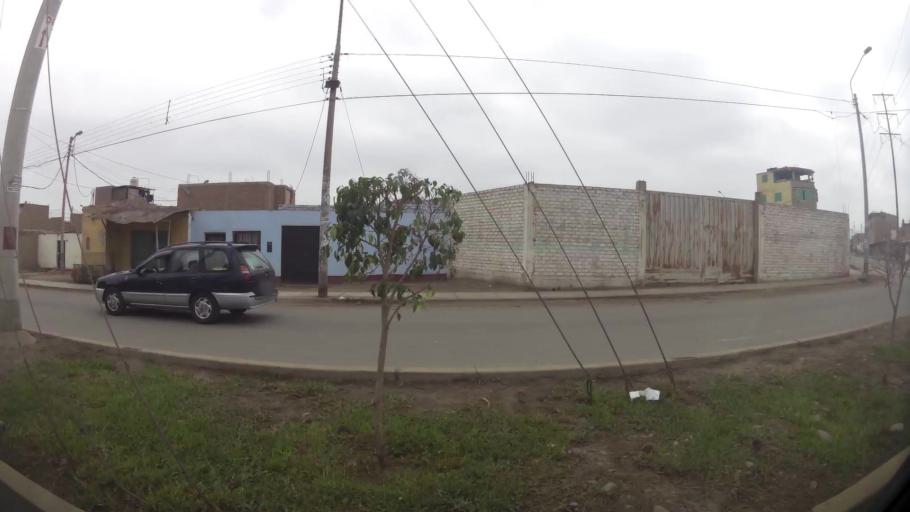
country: PE
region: Lima
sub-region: Provincia de Huaral
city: Huaral
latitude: -11.4989
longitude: -77.1999
